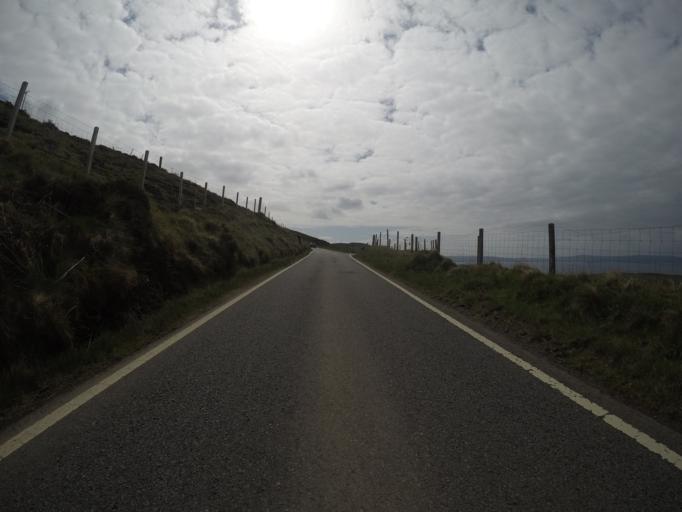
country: GB
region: Scotland
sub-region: Highland
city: Portree
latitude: 57.6072
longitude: -6.3745
